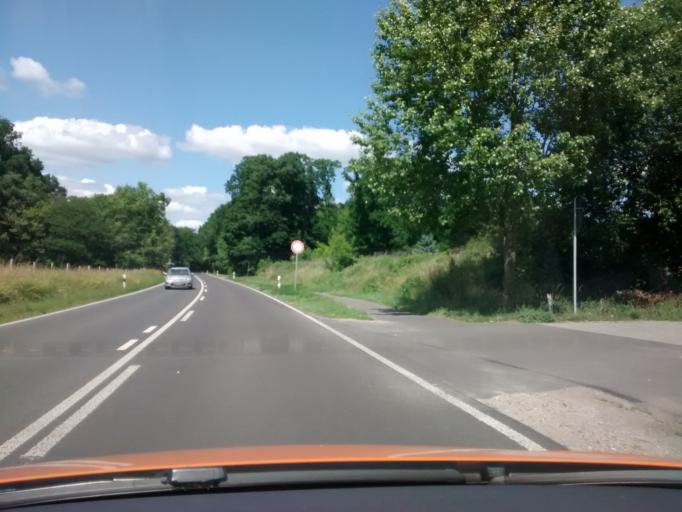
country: DE
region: Berlin
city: Kladow
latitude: 52.4728
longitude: 13.1028
